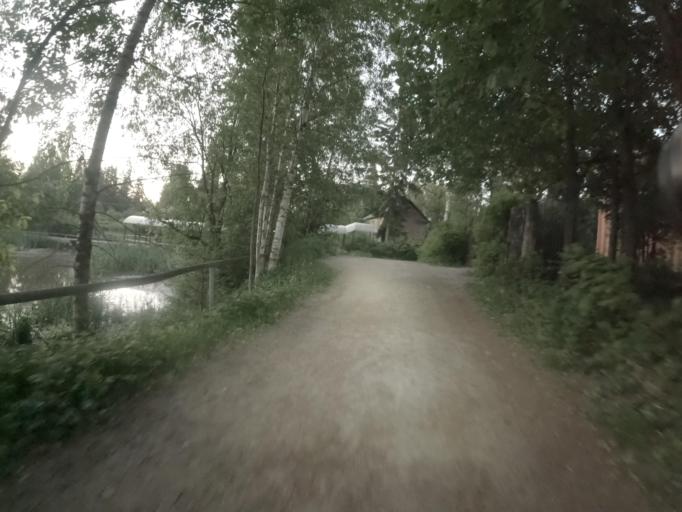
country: RU
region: Leningrad
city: Vsevolozhsk
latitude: 60.0152
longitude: 30.6141
